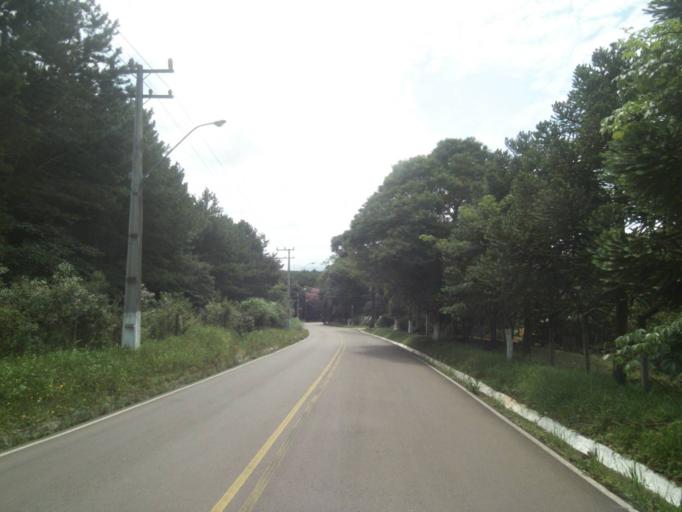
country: BR
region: Parana
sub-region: Campina Grande Do Sul
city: Campina Grande do Sul
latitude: -25.3148
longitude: -49.0243
